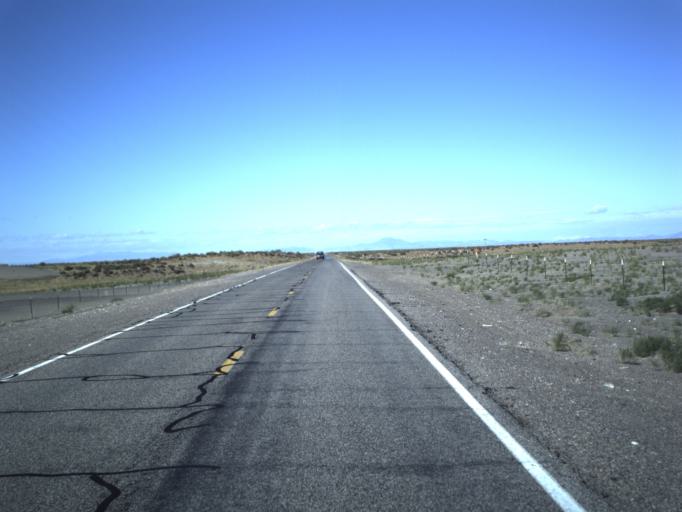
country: US
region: Utah
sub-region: Millard County
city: Delta
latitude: 39.3545
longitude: -112.4043
